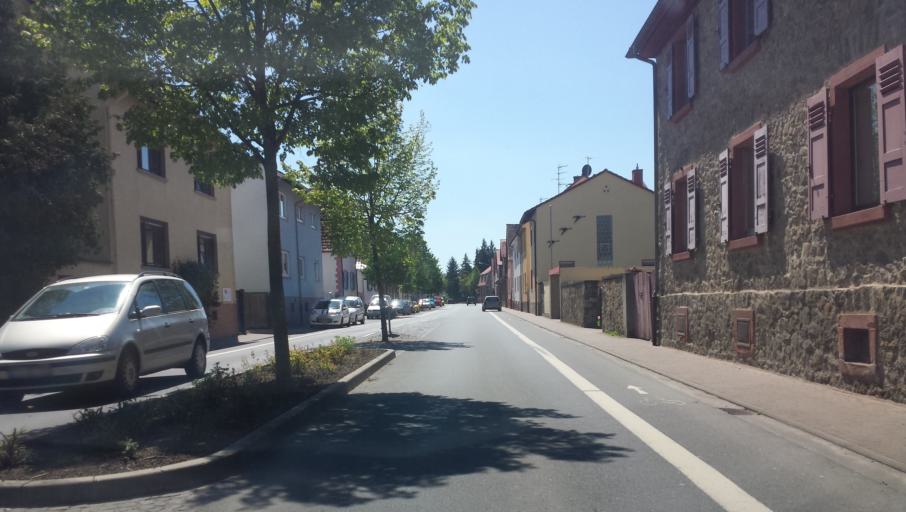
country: DE
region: Hesse
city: Gross-Umstadt
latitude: 49.8635
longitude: 8.9300
